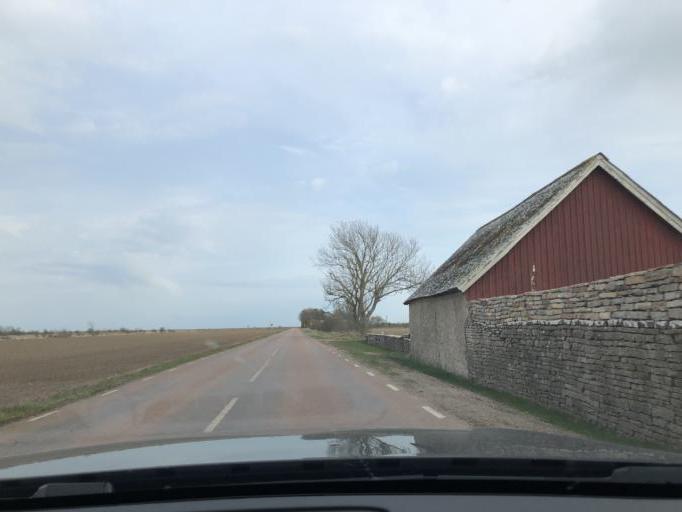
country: SE
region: Kalmar
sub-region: Morbylanga Kommun
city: Moerbylanga
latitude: 56.2886
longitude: 16.4816
